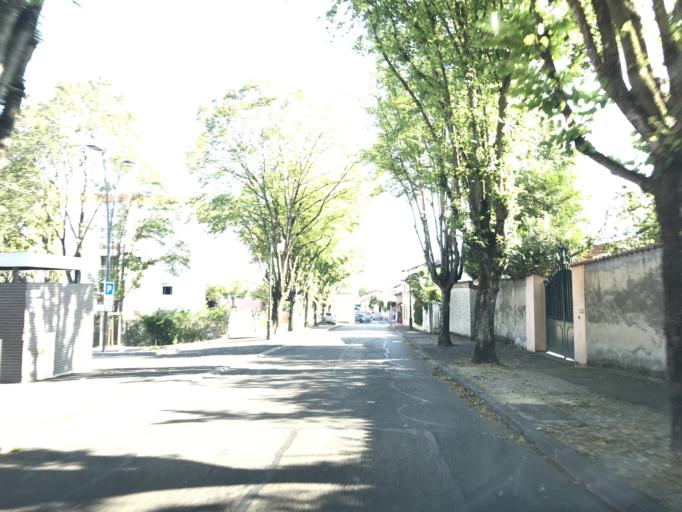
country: FR
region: Rhone-Alpes
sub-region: Departement du Rhone
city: Mions
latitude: 45.6617
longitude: 4.9591
